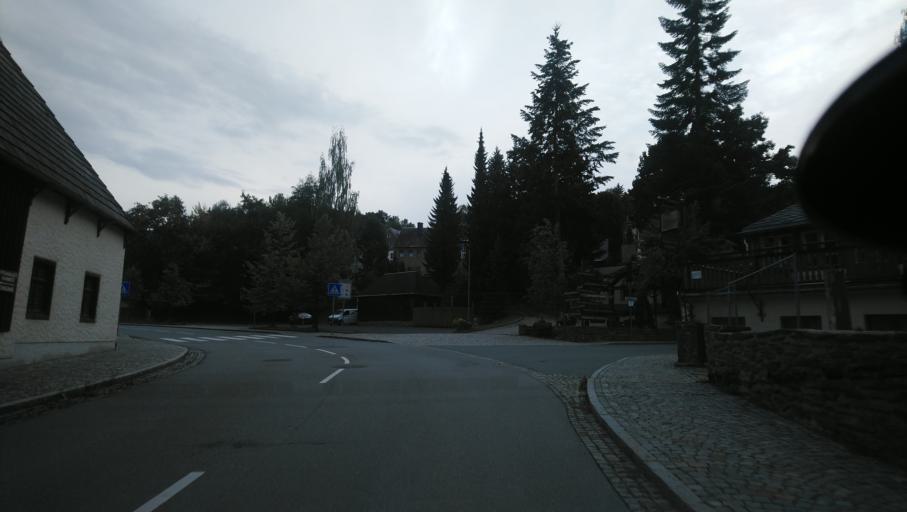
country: DE
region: Saxony
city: Annaberg-Buchholz
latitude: 50.5818
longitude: 12.9954
